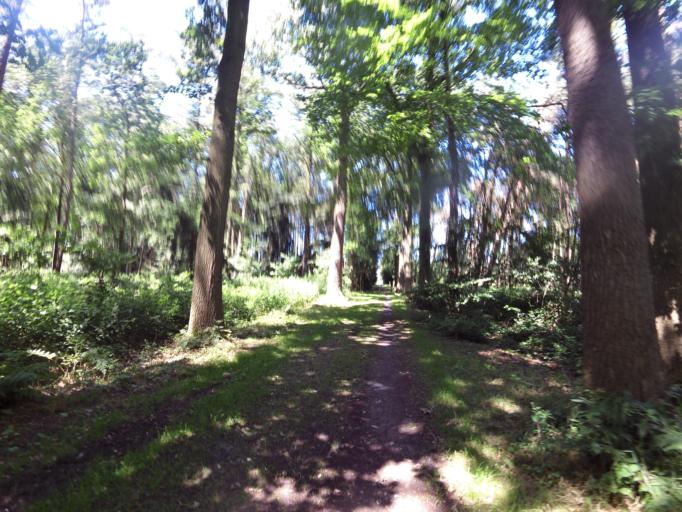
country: BE
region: Flanders
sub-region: Provincie West-Vlaanderen
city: Torhout
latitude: 51.0943
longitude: 3.0744
